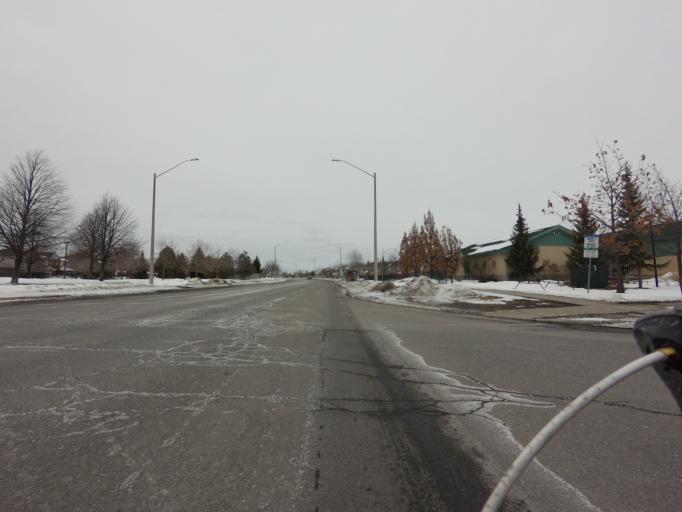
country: CA
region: Ontario
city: Ottawa
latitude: 45.2772
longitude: -75.6881
